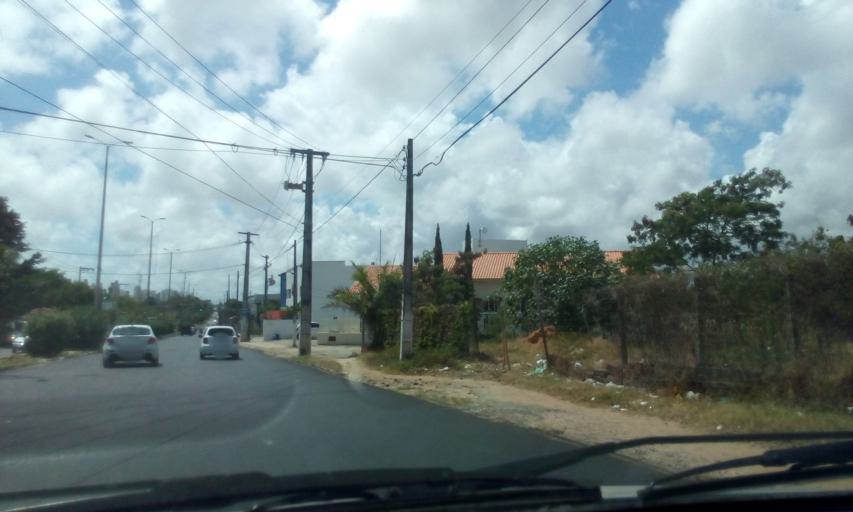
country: BR
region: Rio Grande do Norte
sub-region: Natal
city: Natal
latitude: -5.8614
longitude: -35.2055
